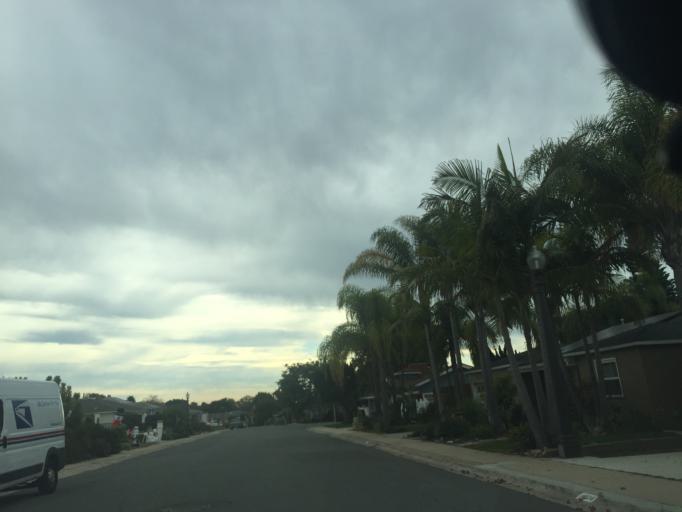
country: US
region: California
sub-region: San Diego County
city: Lemon Grove
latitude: 32.7651
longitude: -117.0898
